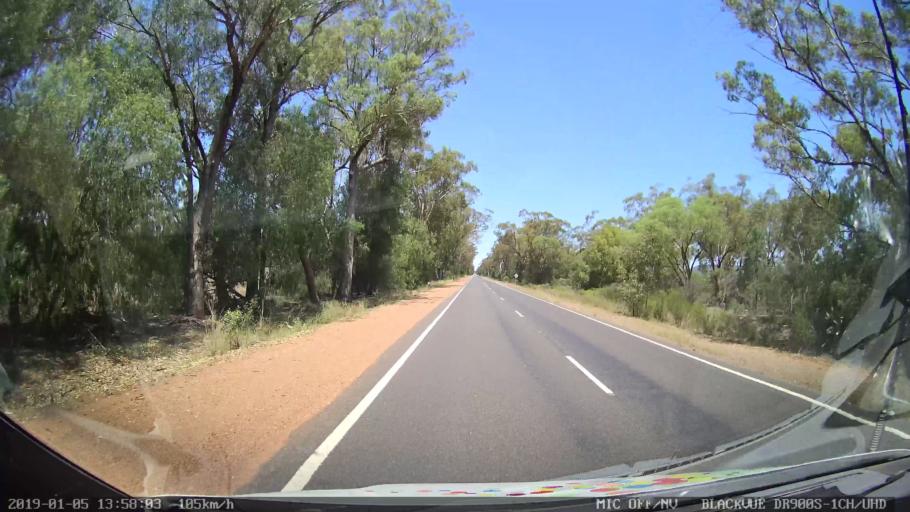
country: AU
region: New South Wales
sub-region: Gunnedah
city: Gunnedah
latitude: -31.1346
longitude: 150.2801
